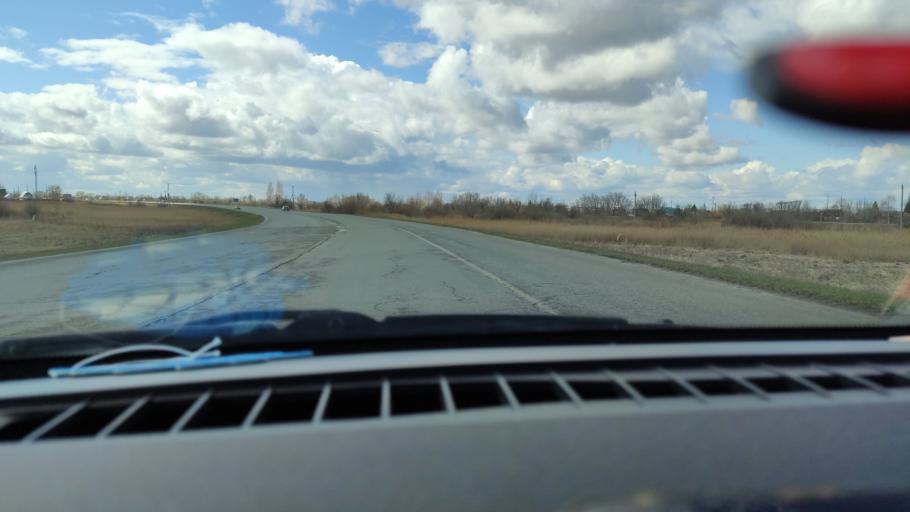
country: RU
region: Samara
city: Tol'yatti
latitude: 53.7153
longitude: 49.4243
